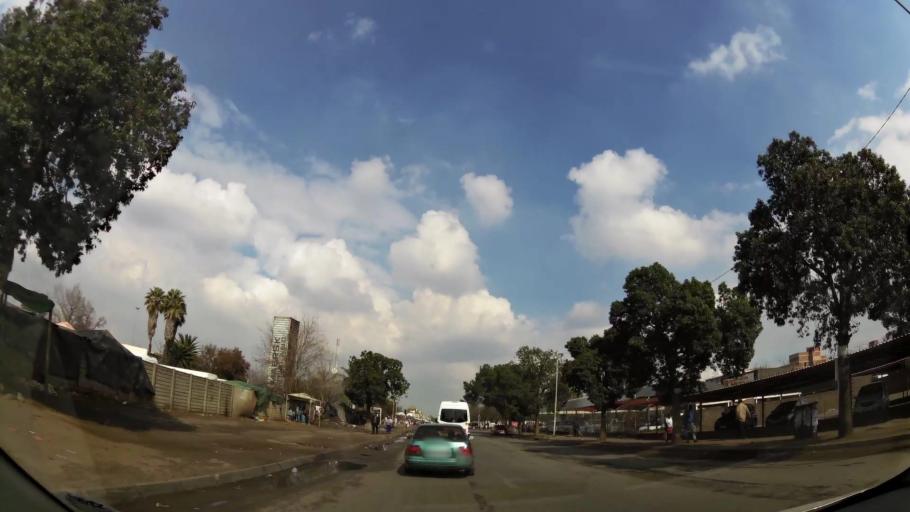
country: ZA
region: Gauteng
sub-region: Sedibeng District Municipality
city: Vereeniging
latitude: -26.6733
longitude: 27.9341
